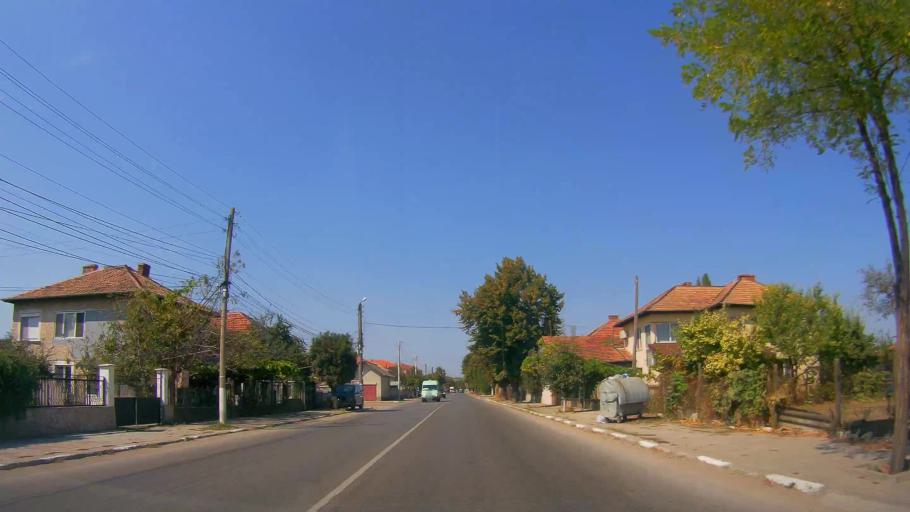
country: BG
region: Razgrad
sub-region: Obshtina Tsar Kaloyan
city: Tsar Kaloyan
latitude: 43.6042
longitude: 26.2423
